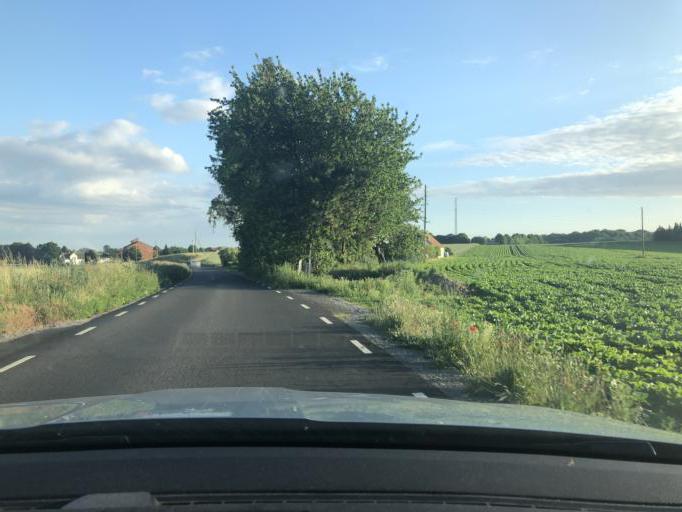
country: SE
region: Skane
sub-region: Simrishamns Kommun
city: Simrishamn
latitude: 55.4657
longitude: 14.1906
